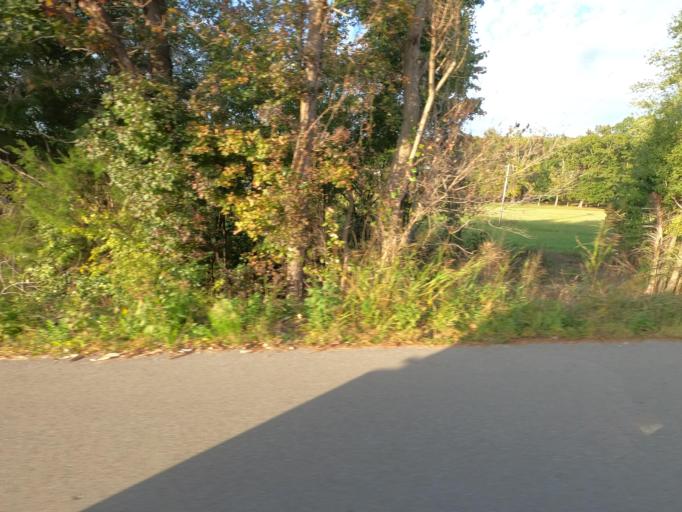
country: US
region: Tennessee
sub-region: Humphreys County
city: Waverly
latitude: 35.8822
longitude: -87.7983
